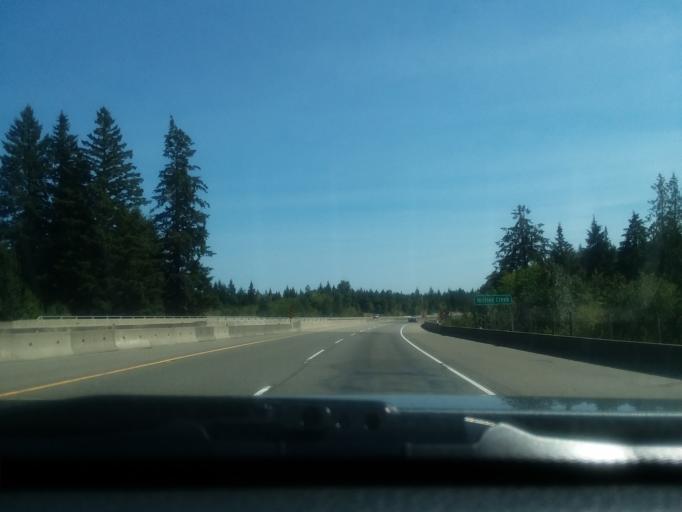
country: CA
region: British Columbia
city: Port Alberni
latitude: 49.4857
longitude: -124.8162
